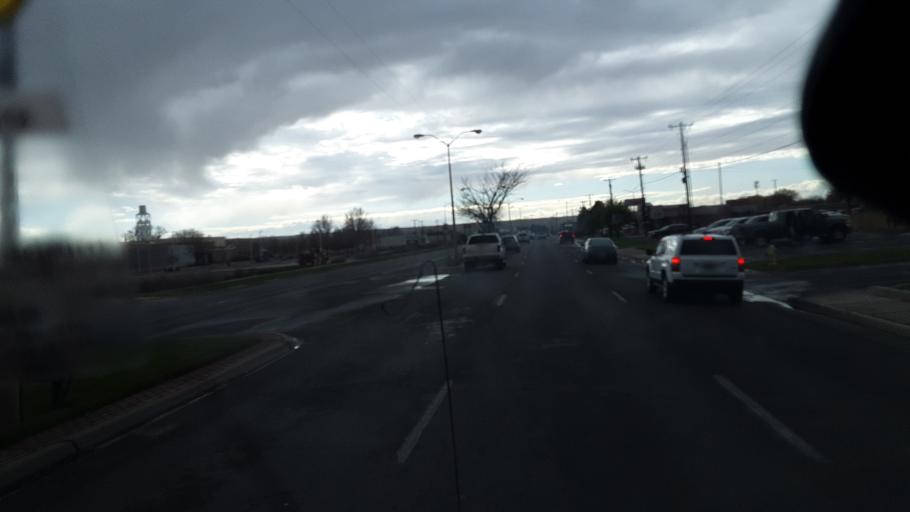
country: US
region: New Mexico
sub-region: San Juan County
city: Farmington
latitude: 36.7466
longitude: -108.1635
